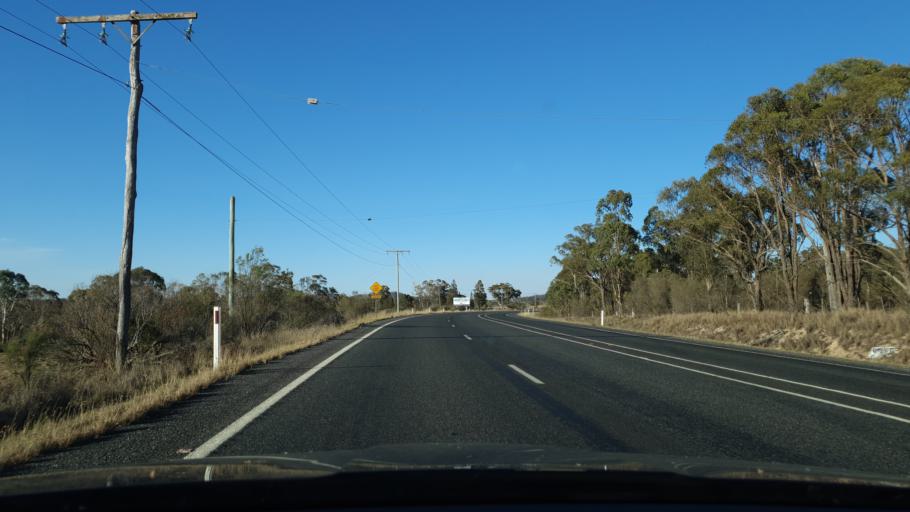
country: AU
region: Queensland
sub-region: Southern Downs
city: Stanthorpe
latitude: -28.6929
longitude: 151.9075
